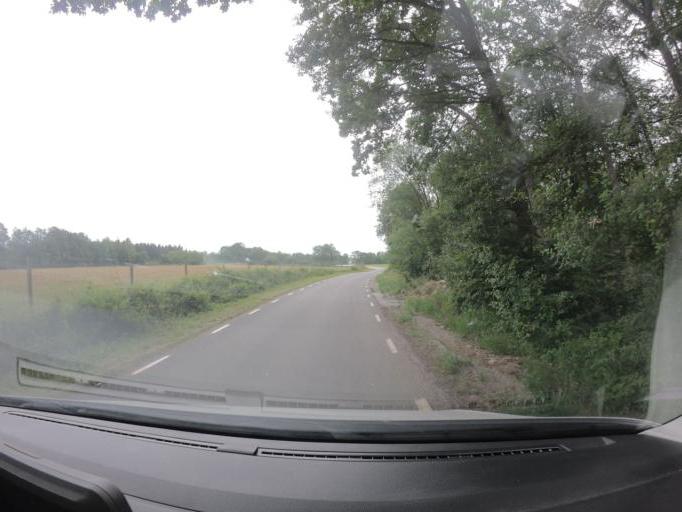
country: SE
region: Skane
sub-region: Hassleholms Kommun
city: Sosdala
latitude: 56.1185
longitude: 13.6429
